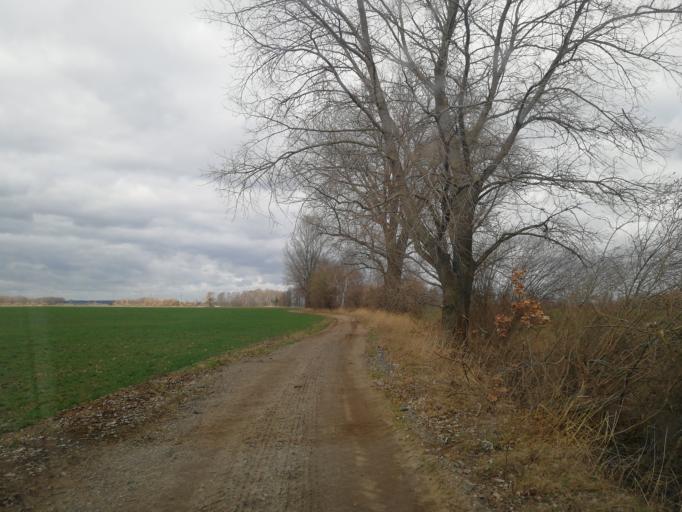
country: DE
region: Brandenburg
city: Schonewalde
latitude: 51.6673
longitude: 13.5629
